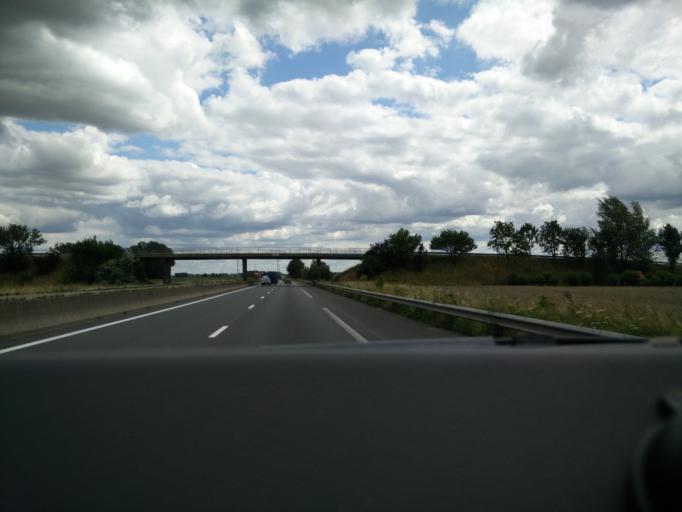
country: FR
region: Nord-Pas-de-Calais
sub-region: Departement du Nord
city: Quaedypre
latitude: 50.9205
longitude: 2.4771
